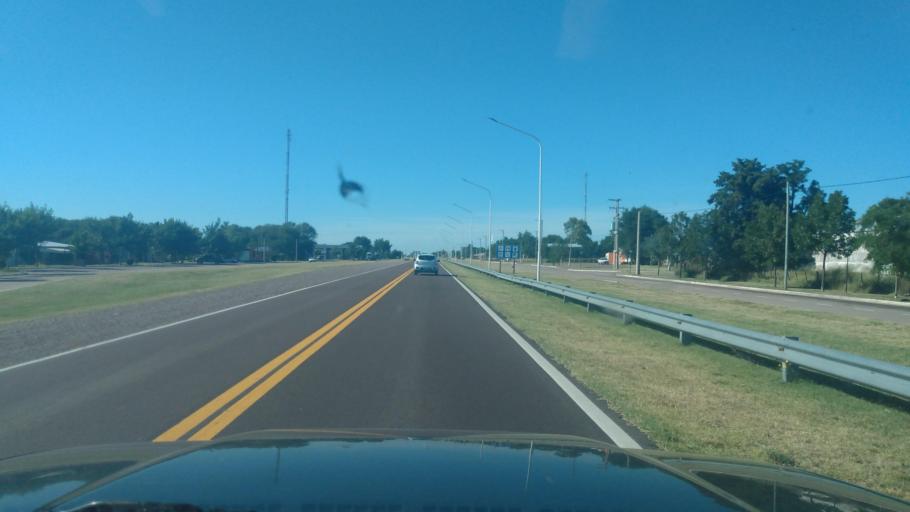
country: AR
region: La Pampa
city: Doblas
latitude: -37.0283
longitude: -64.2889
